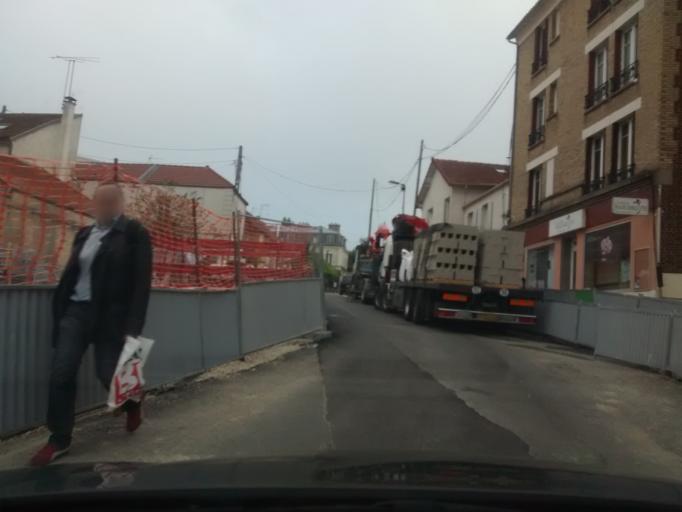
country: FR
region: Ile-de-France
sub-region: Departement des Yvelines
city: Viroflay
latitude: 48.8057
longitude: 2.1690
